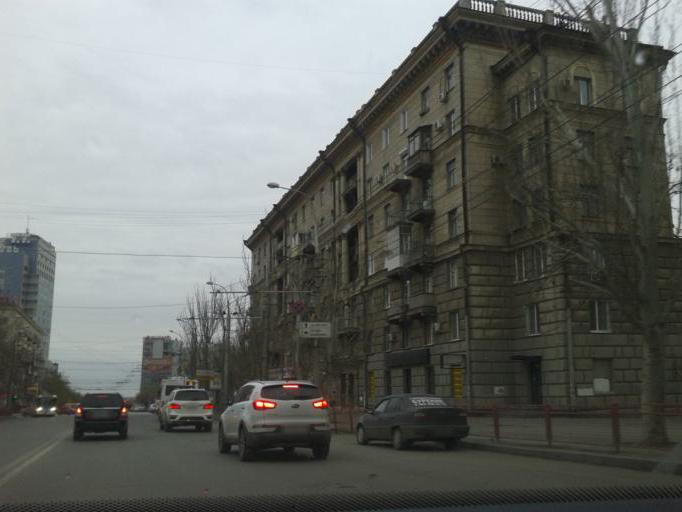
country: RU
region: Volgograd
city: Volgograd
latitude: 48.7102
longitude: 44.5190
